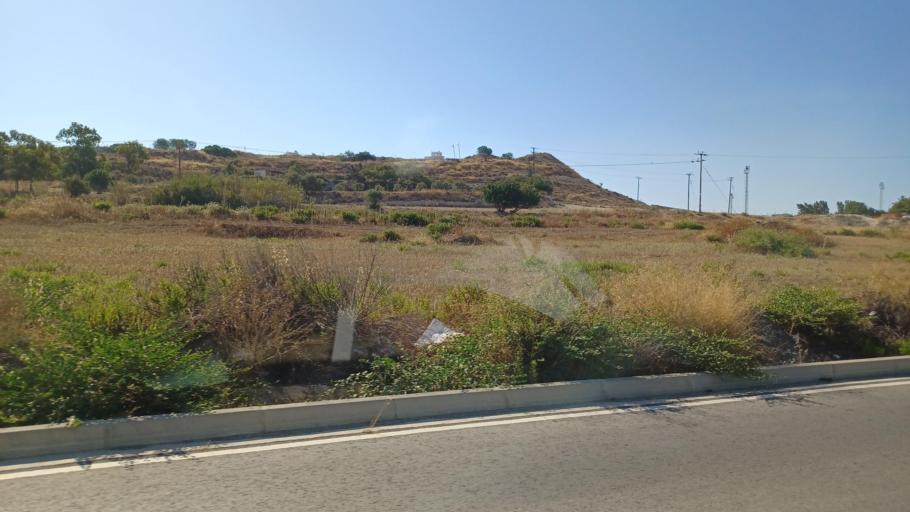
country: CY
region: Larnaka
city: Pyla
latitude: 35.0009
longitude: 33.6922
